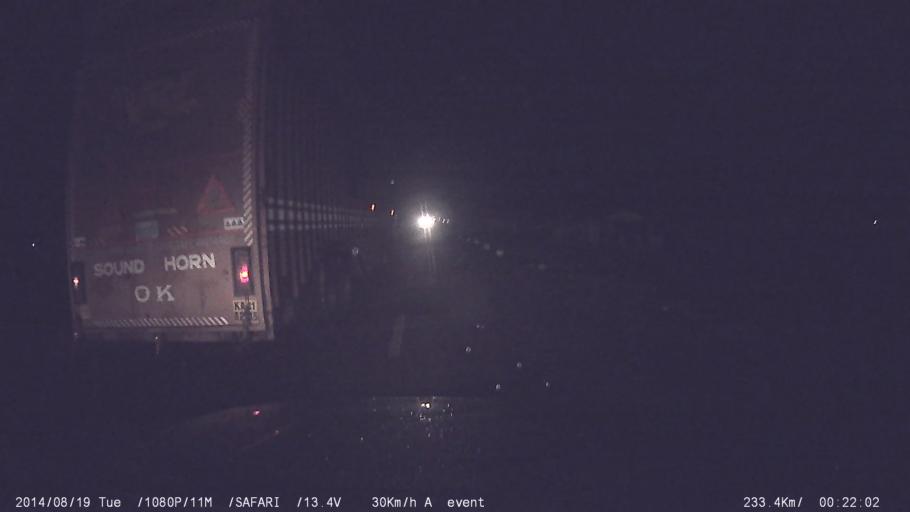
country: IN
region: Kerala
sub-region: Palakkad district
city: Palakkad
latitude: 10.7982
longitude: 76.7445
